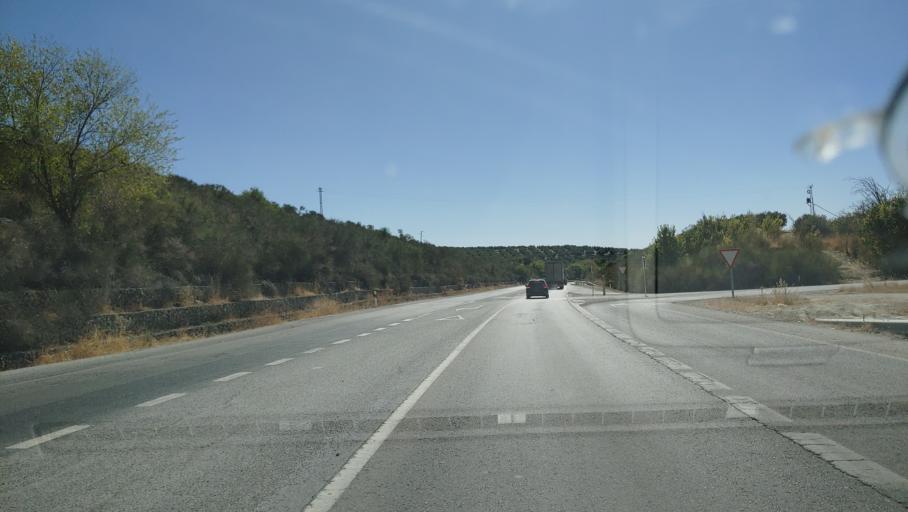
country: ES
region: Andalusia
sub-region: Provincia de Jaen
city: Villacarrillo
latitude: 38.1056
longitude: -3.1018
